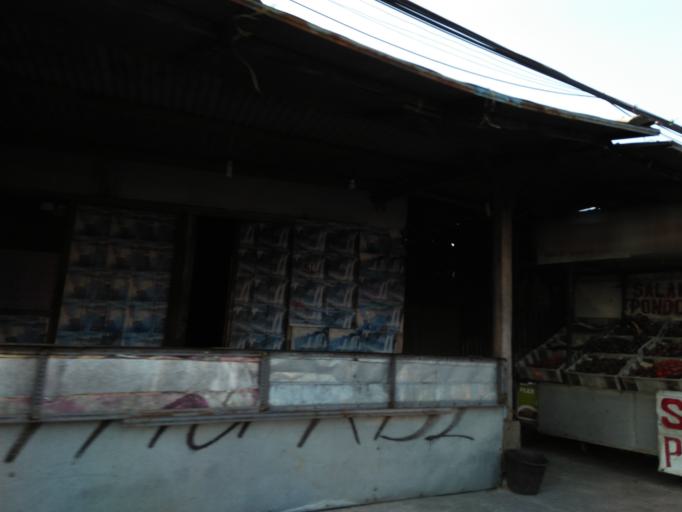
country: ID
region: Daerah Istimewa Yogyakarta
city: Depok
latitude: -7.7737
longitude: 110.4651
